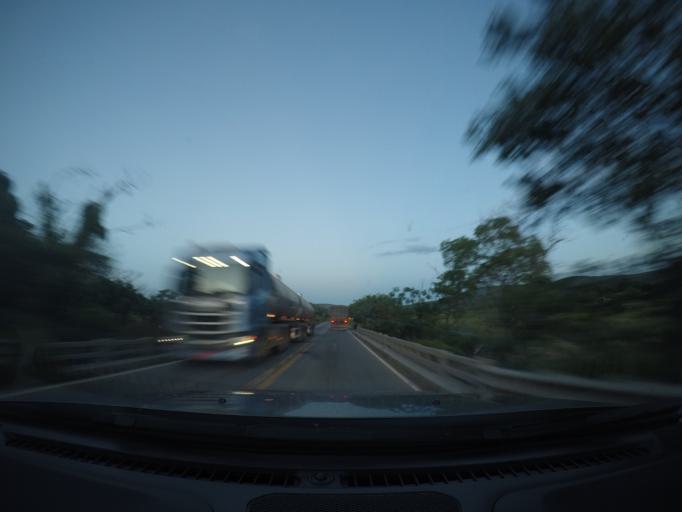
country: BR
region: Bahia
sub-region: Seabra
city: Seabra
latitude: -12.4885
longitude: -41.7295
